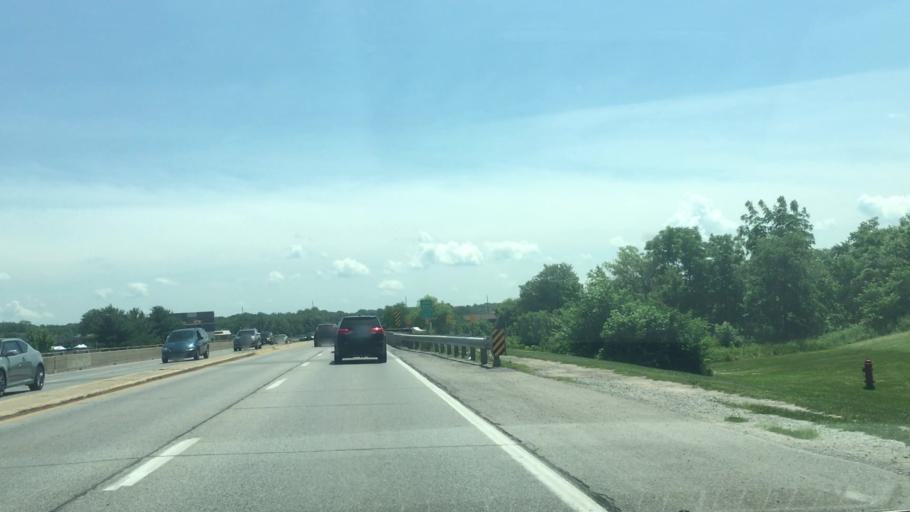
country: US
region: Iowa
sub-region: Johnson County
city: Iowa City
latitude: 41.6473
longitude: -91.5363
